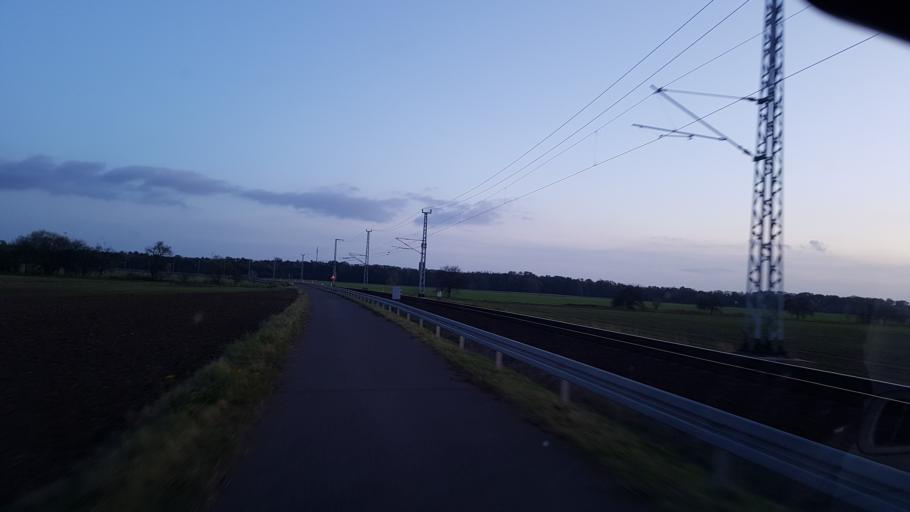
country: DE
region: Brandenburg
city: Doberlug-Kirchhain
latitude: 51.6412
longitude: 13.5774
